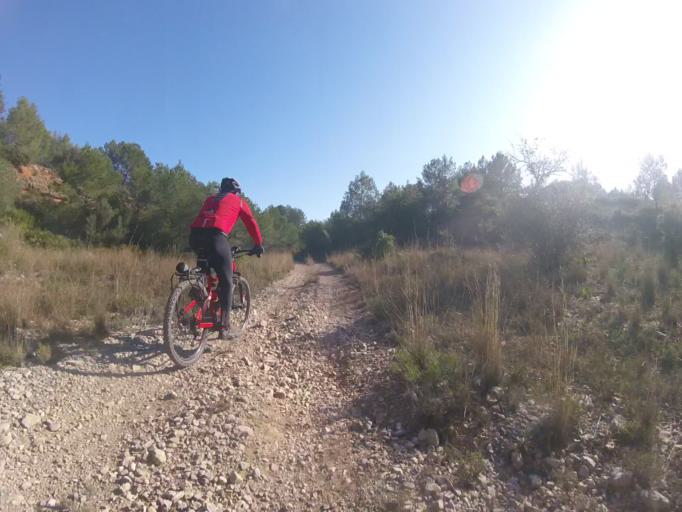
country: ES
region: Valencia
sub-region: Provincia de Castello
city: Santa Magdalena de Pulpis
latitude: 40.3071
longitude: 0.3365
